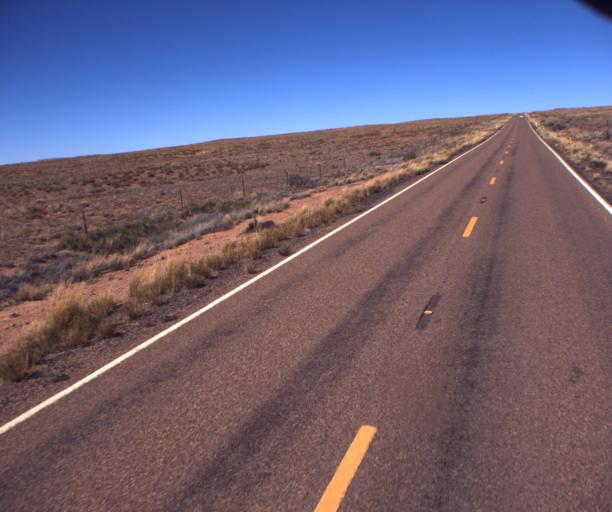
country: US
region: Arizona
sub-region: Navajo County
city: Holbrook
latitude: 34.9948
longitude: -110.0892
